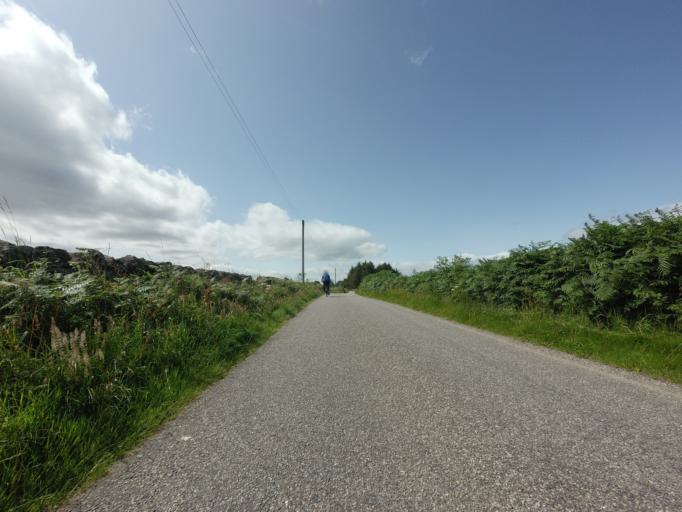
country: GB
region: Scotland
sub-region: Highland
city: Fortrose
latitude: 57.4912
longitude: -4.0147
